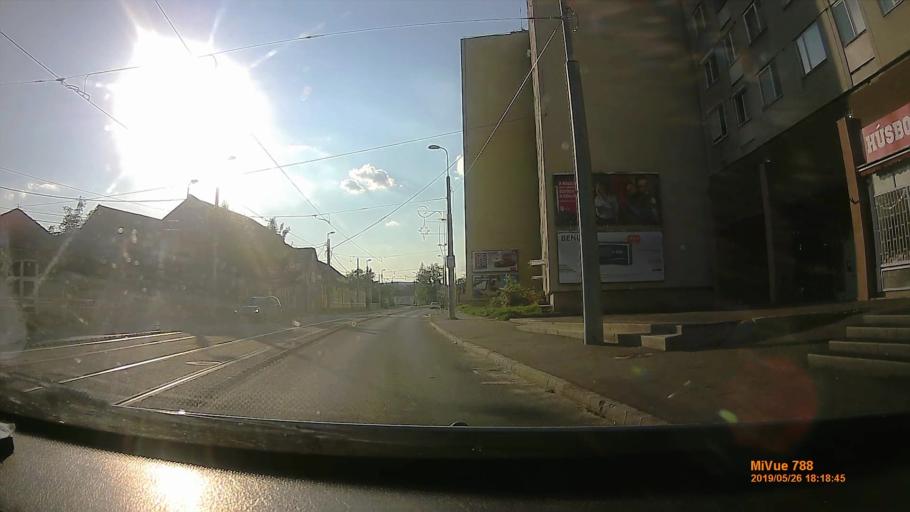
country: HU
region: Borsod-Abauj-Zemplen
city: Sajobabony
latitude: 48.1024
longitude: 20.6865
